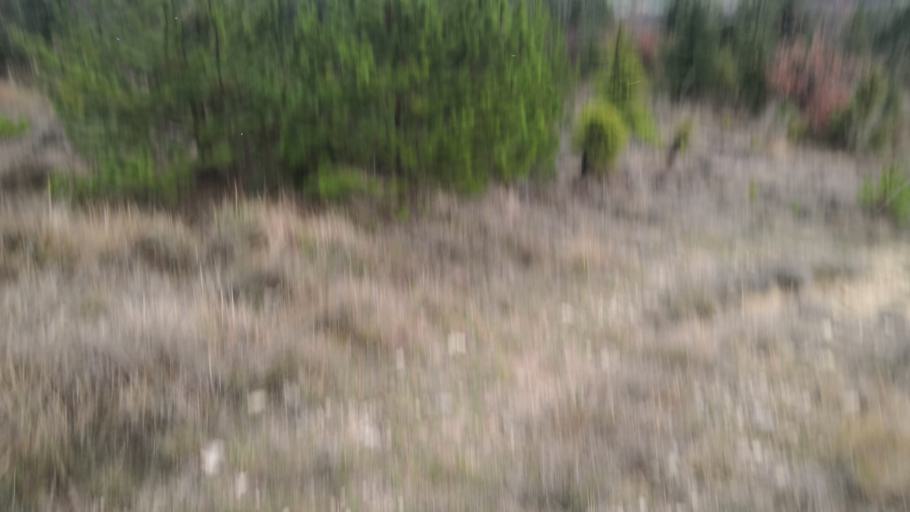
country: FR
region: Rhone-Alpes
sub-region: Departement de la Drome
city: Chateauneuf-du-Rhone
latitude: 44.4712
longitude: 4.7240
